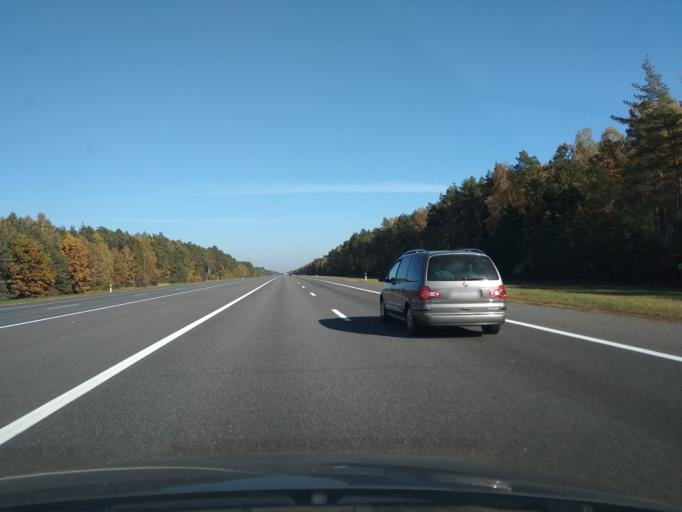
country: BY
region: Brest
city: Ivatsevichy
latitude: 52.7473
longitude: 25.4939
